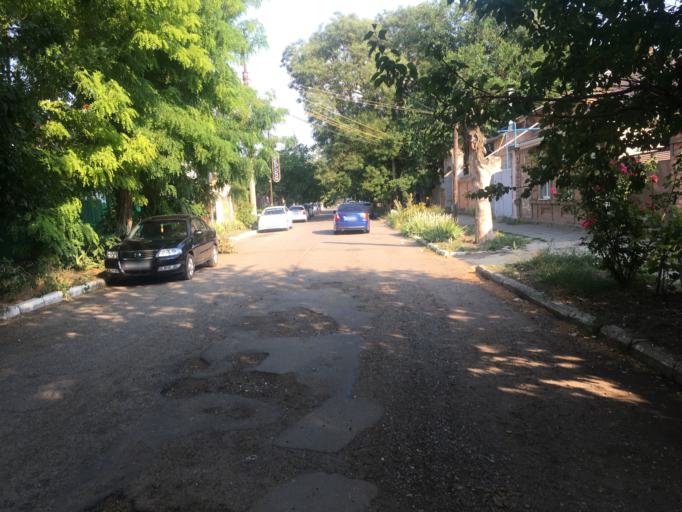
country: RU
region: Krasnodarskiy
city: Yeysk
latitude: 46.7160
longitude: 38.2719
